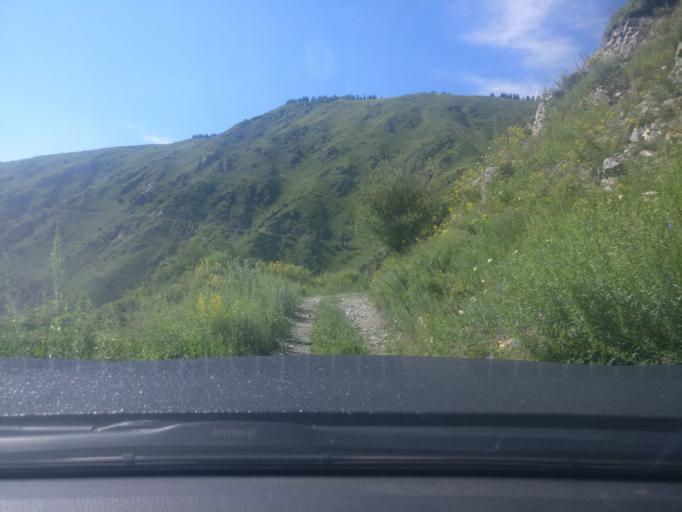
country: KZ
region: Almaty Qalasy
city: Almaty
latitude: 43.1024
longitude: 76.9506
